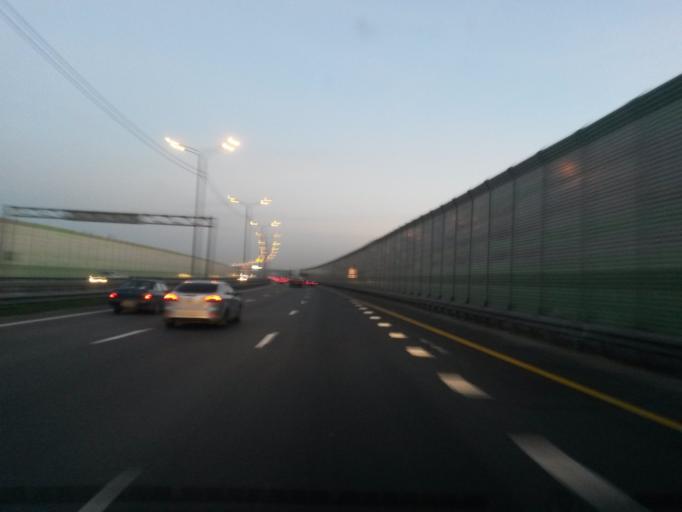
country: RU
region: Moskovskaya
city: Belyye Stolby
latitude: 55.3209
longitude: 37.8127
